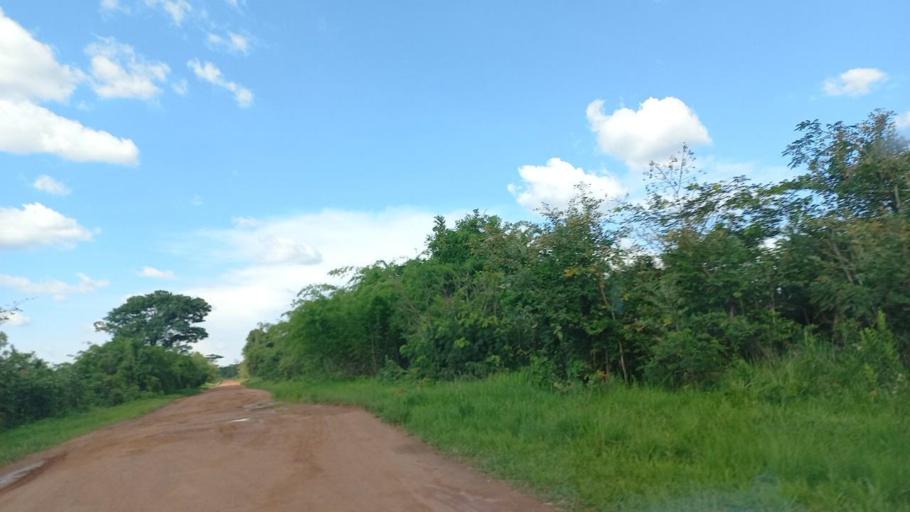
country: ZM
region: Copperbelt
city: Kitwe
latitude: -12.8499
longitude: 28.3914
